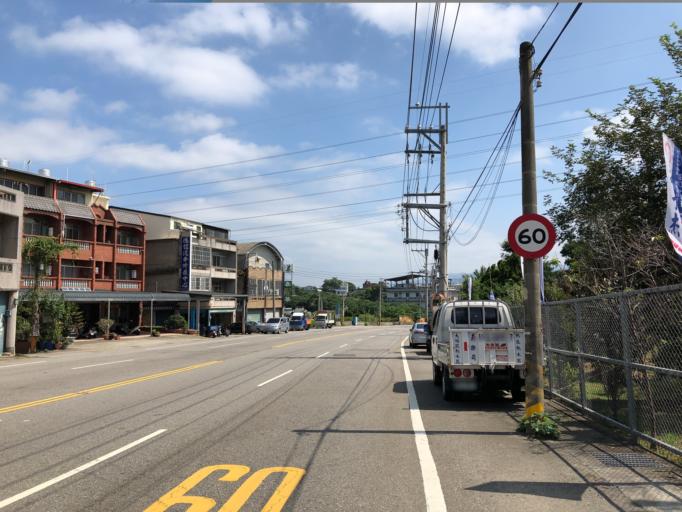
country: TW
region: Taiwan
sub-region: Miaoli
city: Miaoli
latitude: 24.5795
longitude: 120.8610
